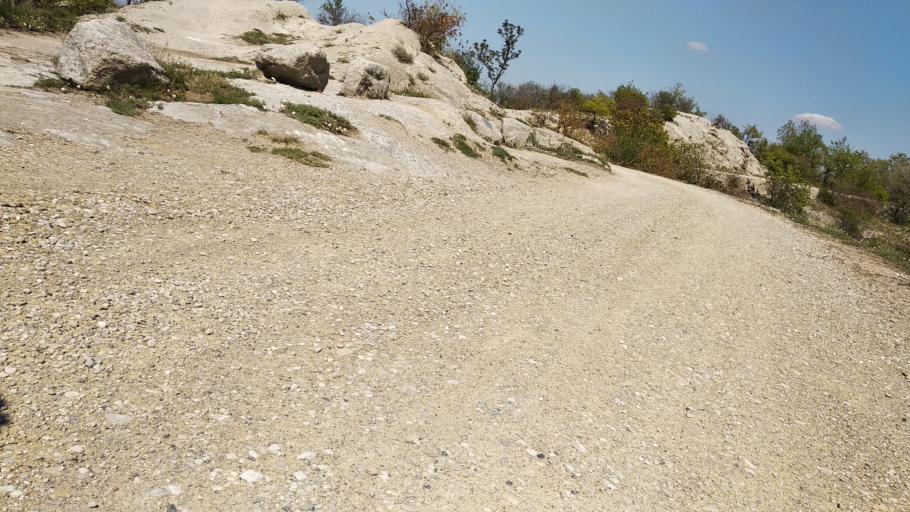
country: IT
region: Emilia-Romagna
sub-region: Provincia di Ravenna
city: Riolo Terme
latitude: 44.2367
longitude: 11.6983
